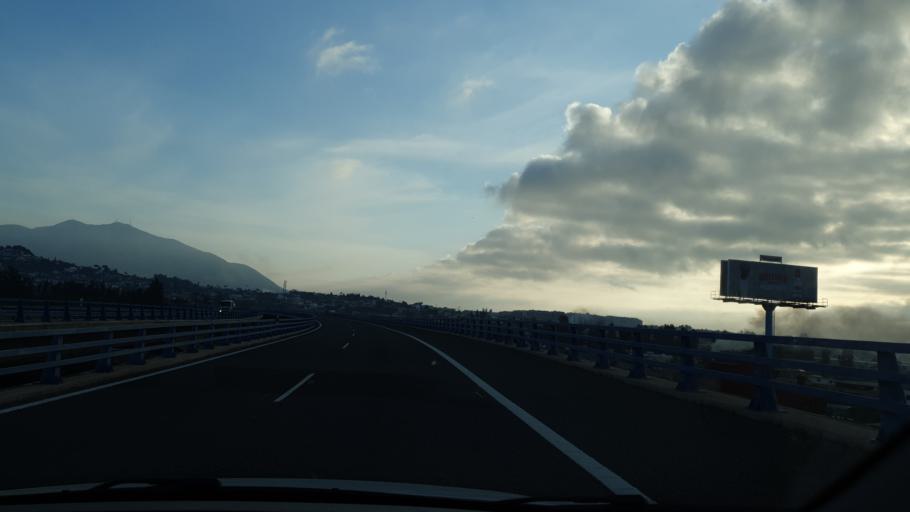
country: ES
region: Andalusia
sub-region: Provincia de Malaga
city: Fuengirola
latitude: 36.5414
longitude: -4.6612
